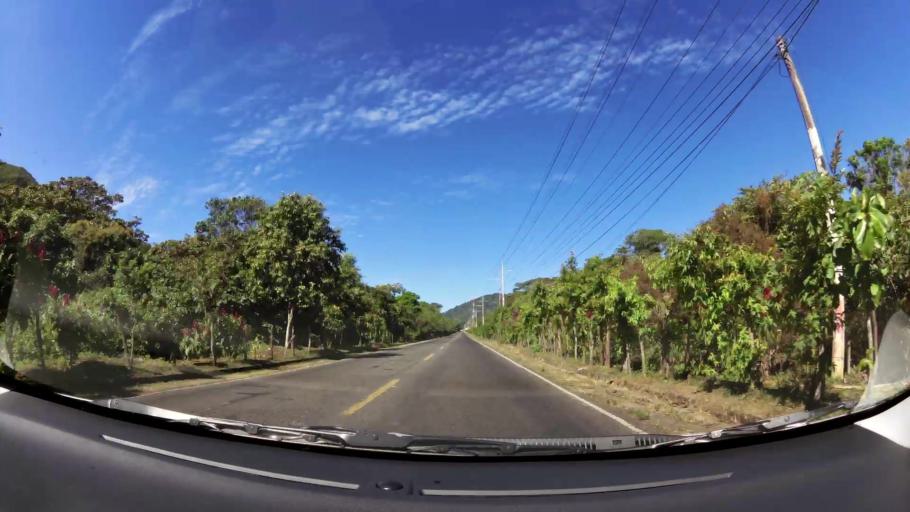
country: SV
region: Sonsonate
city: Juayua
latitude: 13.8607
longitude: -89.7912
